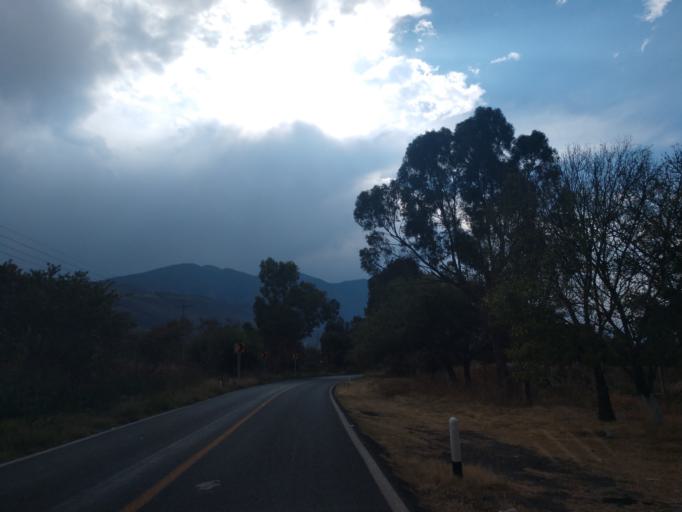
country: MX
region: Jalisco
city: San Juan Cosala
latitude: 20.1937
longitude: -103.2878
